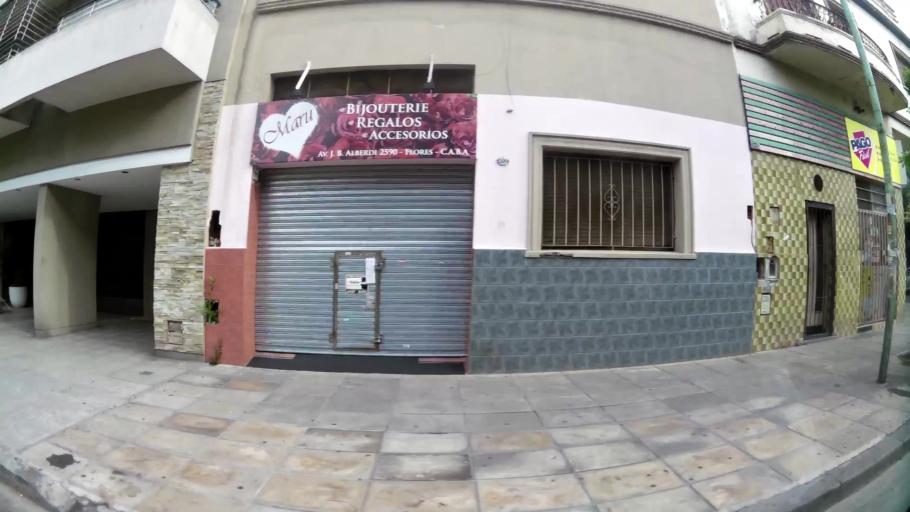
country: AR
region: Buenos Aires F.D.
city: Villa Santa Rita
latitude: -34.6320
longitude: -58.4643
